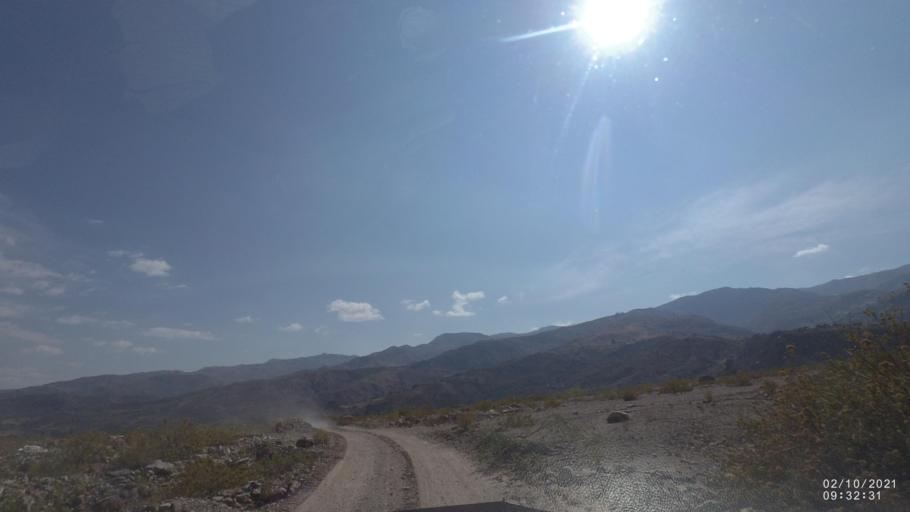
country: BO
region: Cochabamba
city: Irpa Irpa
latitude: -17.8460
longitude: -66.3205
